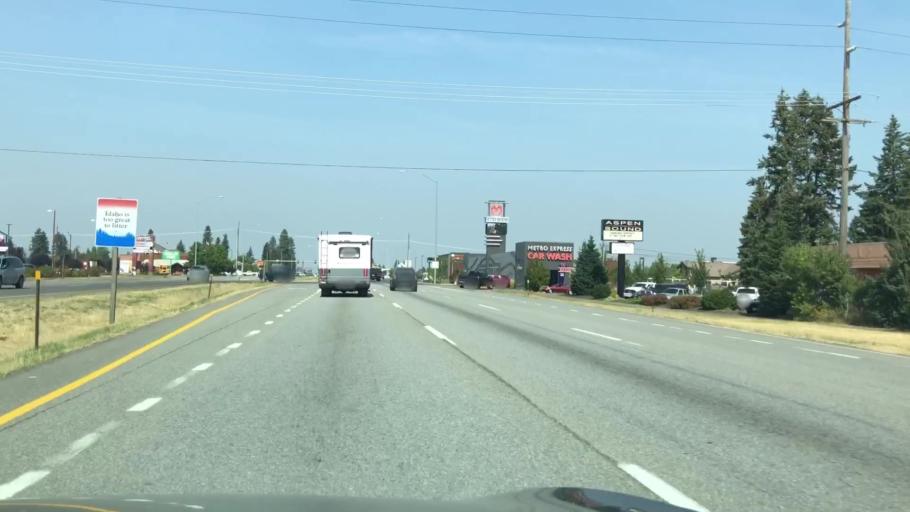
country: US
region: Idaho
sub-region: Kootenai County
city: Coeur d'Alene
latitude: 47.7039
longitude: -116.7915
